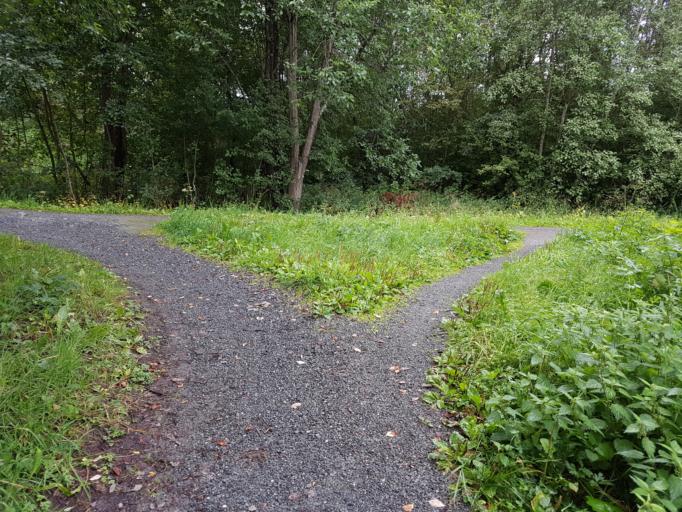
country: NO
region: Sor-Trondelag
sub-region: Trondheim
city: Trondheim
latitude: 63.3963
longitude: 10.4401
